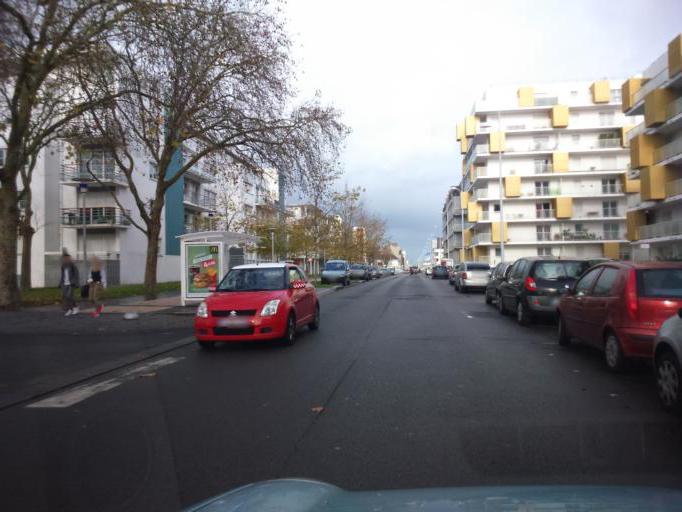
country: FR
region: Pays de la Loire
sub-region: Departement de la Loire-Atlantique
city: Saint-Nazaire
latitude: 47.2744
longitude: -2.2061
